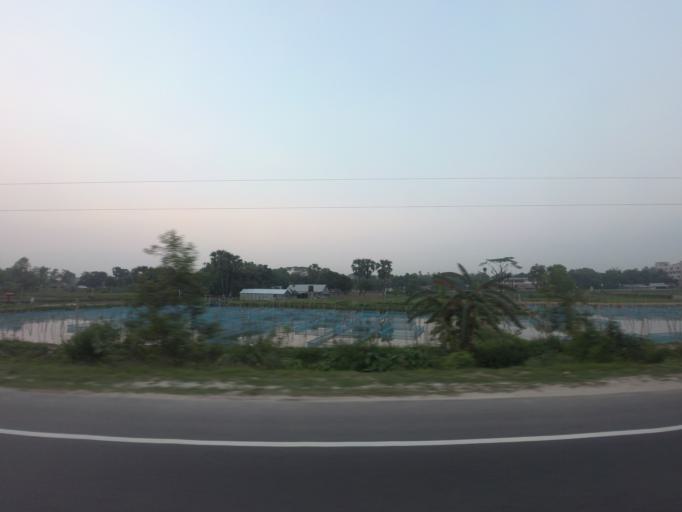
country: BD
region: Chittagong
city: Comilla
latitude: 23.4769
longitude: 91.0904
